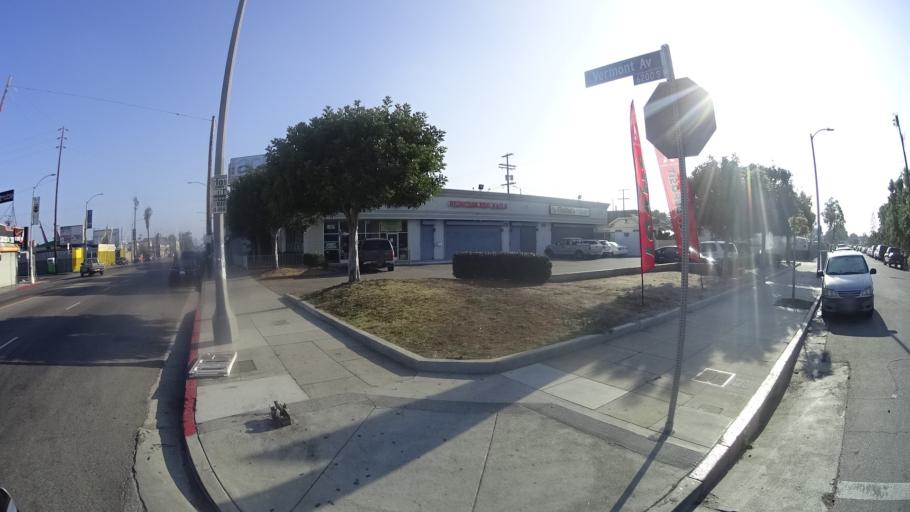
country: US
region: California
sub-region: Los Angeles County
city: Westmont
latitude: 33.9828
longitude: -118.2914
